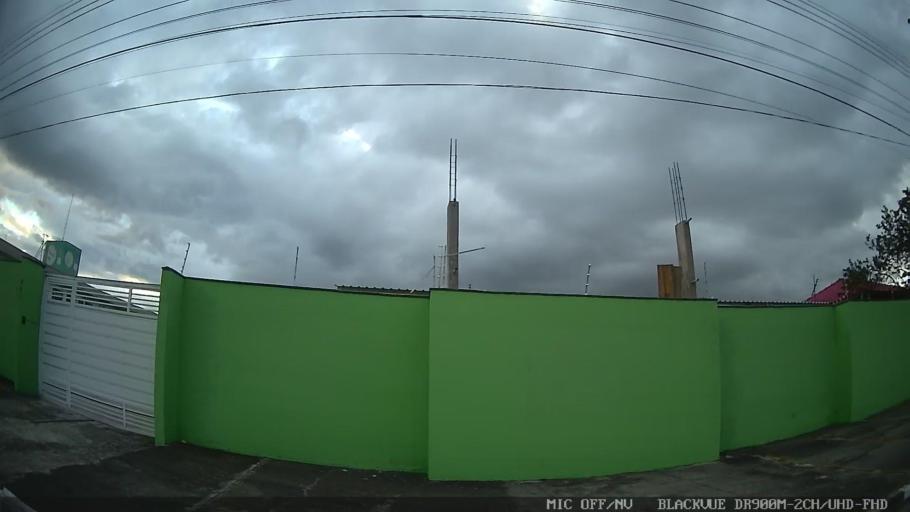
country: BR
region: Sao Paulo
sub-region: Sao Sebastiao
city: Sao Sebastiao
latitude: -23.6938
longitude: -45.4314
